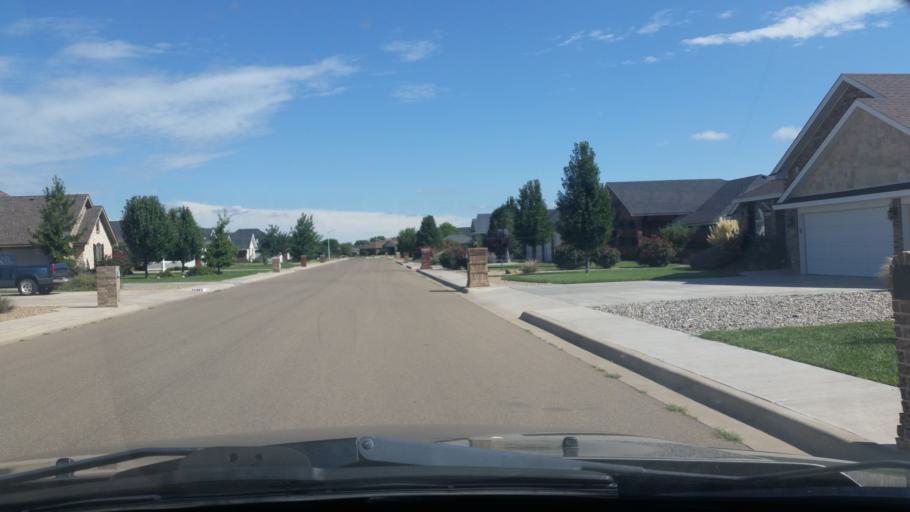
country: US
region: New Mexico
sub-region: Curry County
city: Clovis
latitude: 34.4374
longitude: -103.1744
